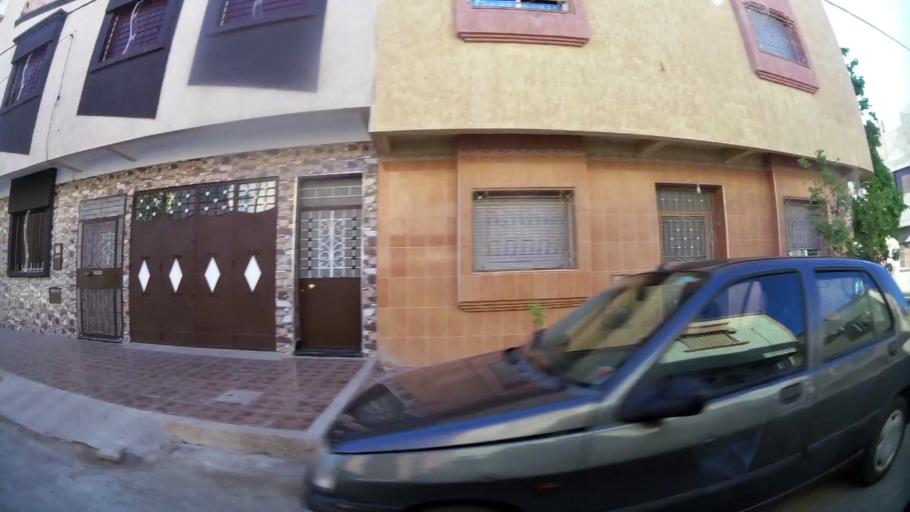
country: MA
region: Oriental
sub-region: Oujda-Angad
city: Oujda
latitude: 34.6750
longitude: -1.9439
